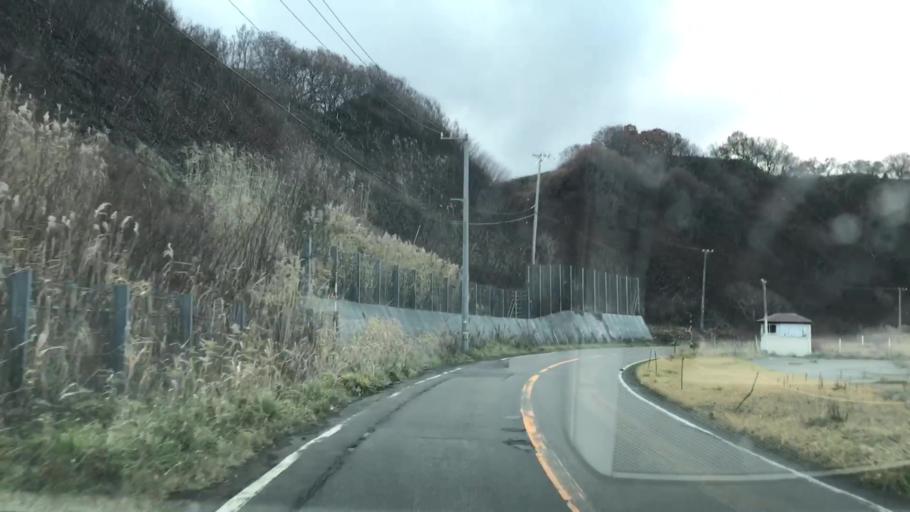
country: JP
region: Hokkaido
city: Yoichi
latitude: 43.3394
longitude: 140.4535
